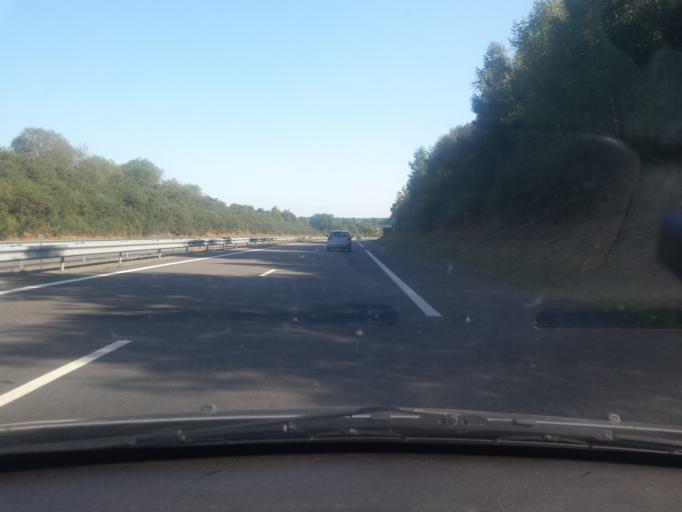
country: FR
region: Brittany
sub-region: Departement du Morbihan
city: Naizin
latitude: 47.9980
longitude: -2.8901
